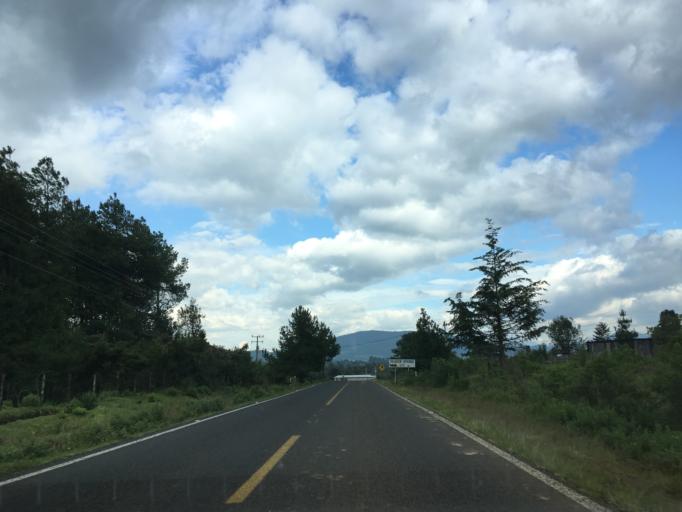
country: MX
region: Michoacan
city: Pichataro
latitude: 19.5838
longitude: -101.8249
